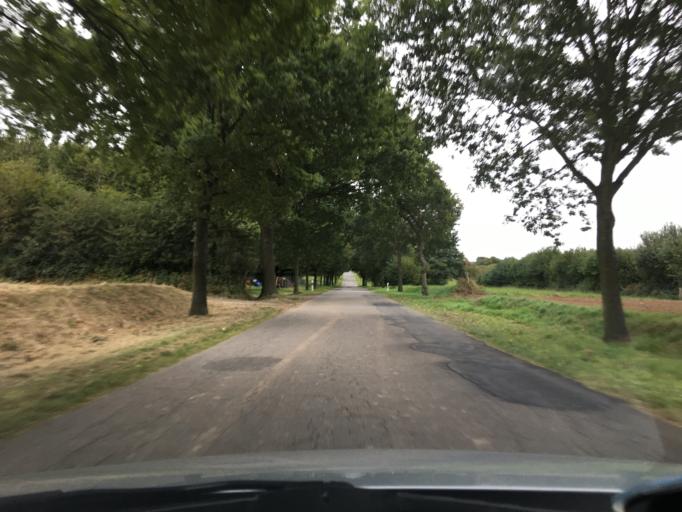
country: DE
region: Schleswig-Holstein
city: Felm
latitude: 54.4692
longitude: 10.0652
